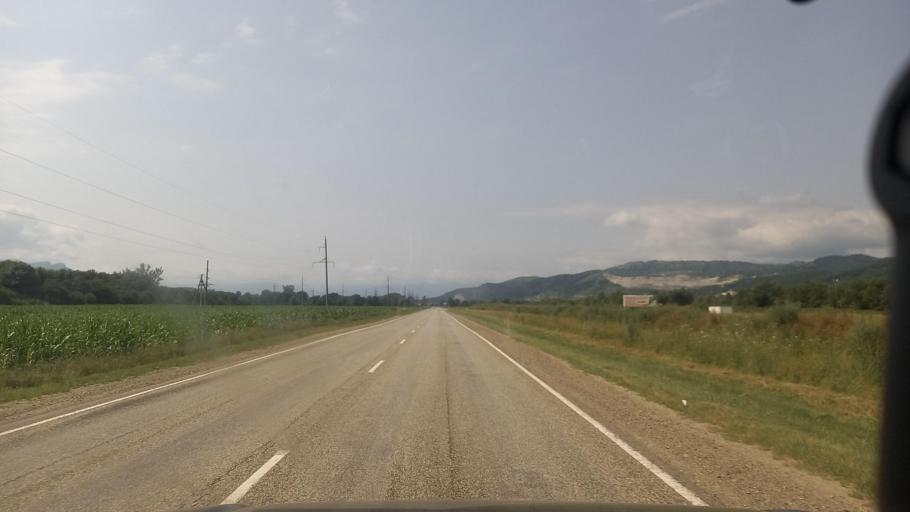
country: RU
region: Krasnodarskiy
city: Shedok
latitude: 44.2004
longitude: 40.8476
